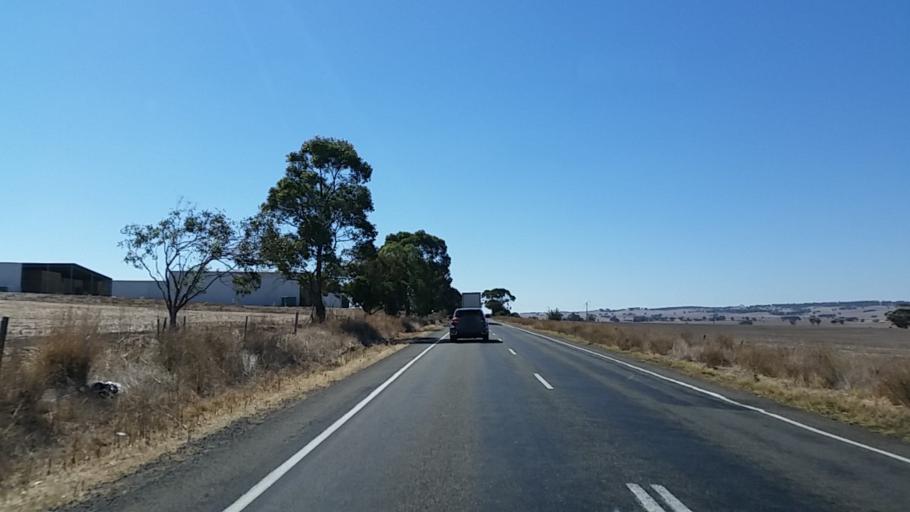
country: AU
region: South Australia
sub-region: Clare and Gilbert Valleys
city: Clare
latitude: -34.0257
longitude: 138.8045
